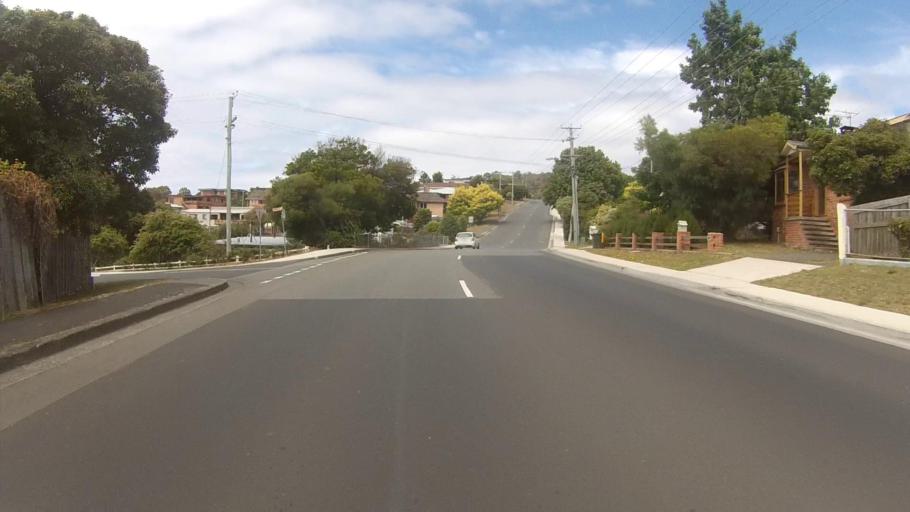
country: AU
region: Tasmania
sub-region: Kingborough
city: Blackmans Bay
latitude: -43.0035
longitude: 147.3190
